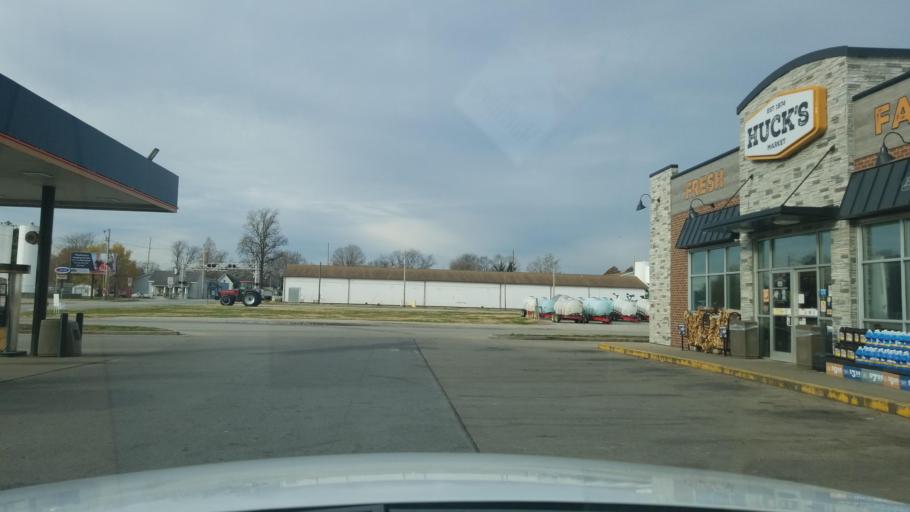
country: US
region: Indiana
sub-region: Posey County
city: Mount Vernon
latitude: 37.9307
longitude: -87.9028
